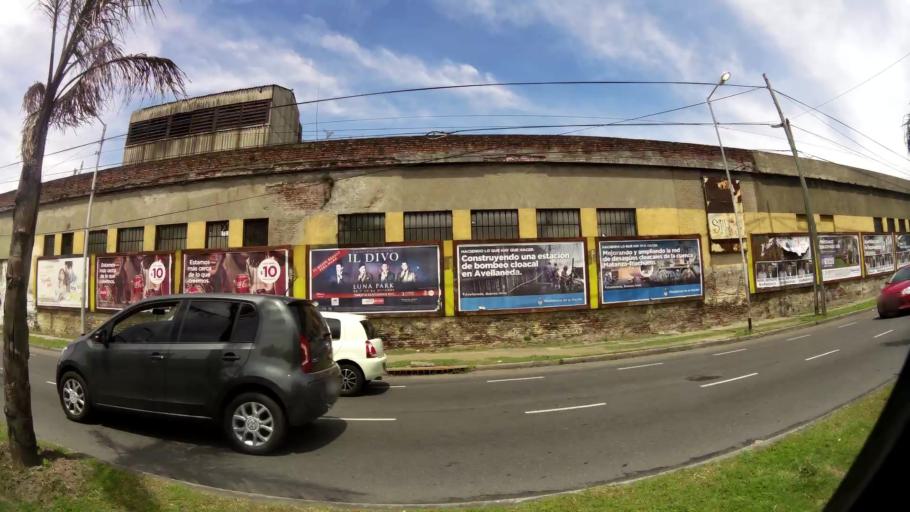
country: AR
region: Buenos Aires
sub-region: Partido de Avellaneda
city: Avellaneda
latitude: -34.6676
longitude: -58.3869
